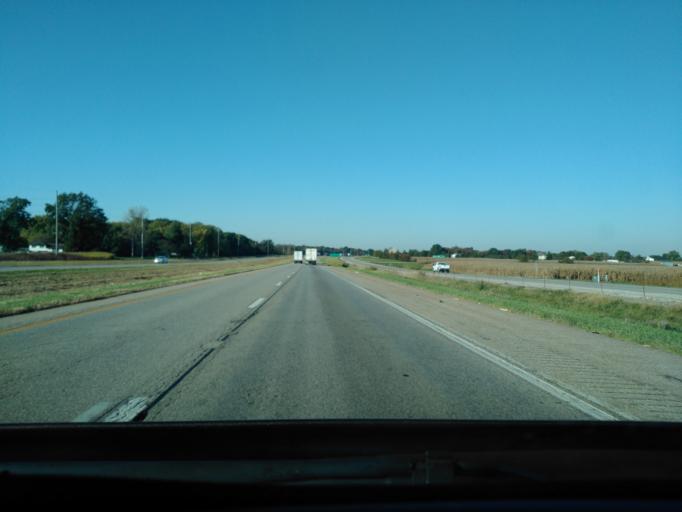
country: US
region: Illinois
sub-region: Bond County
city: Greenville
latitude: 38.8497
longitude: -89.4643
